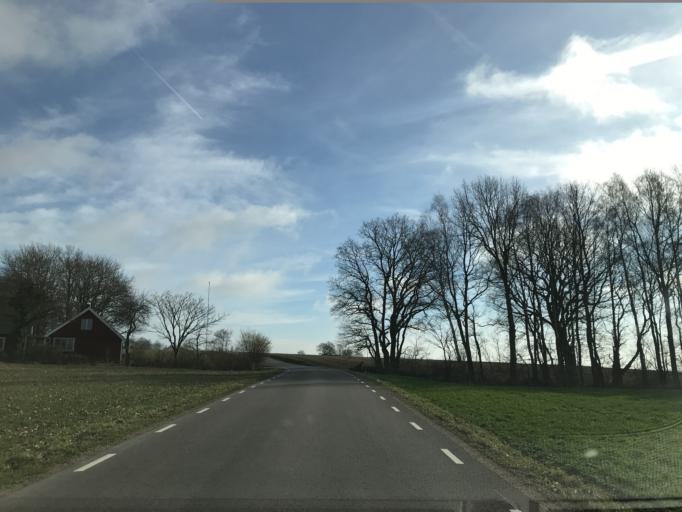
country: SE
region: Skane
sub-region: Hoors Kommun
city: Loberod
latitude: 55.7266
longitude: 13.5050
